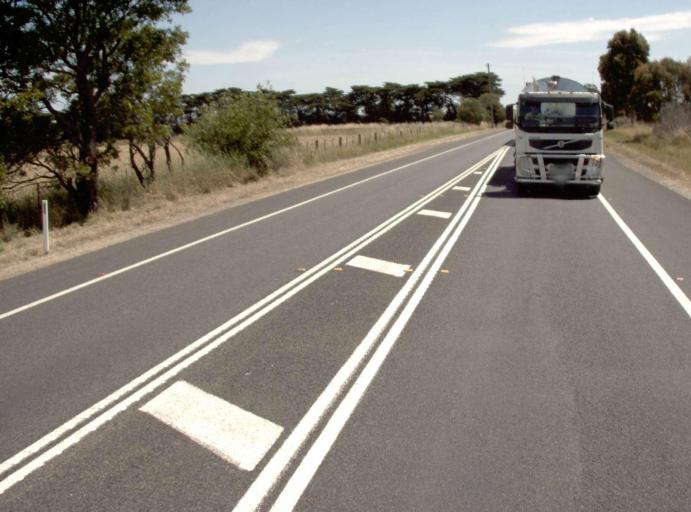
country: AU
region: Victoria
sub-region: Wellington
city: Heyfield
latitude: -38.1204
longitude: 146.8569
